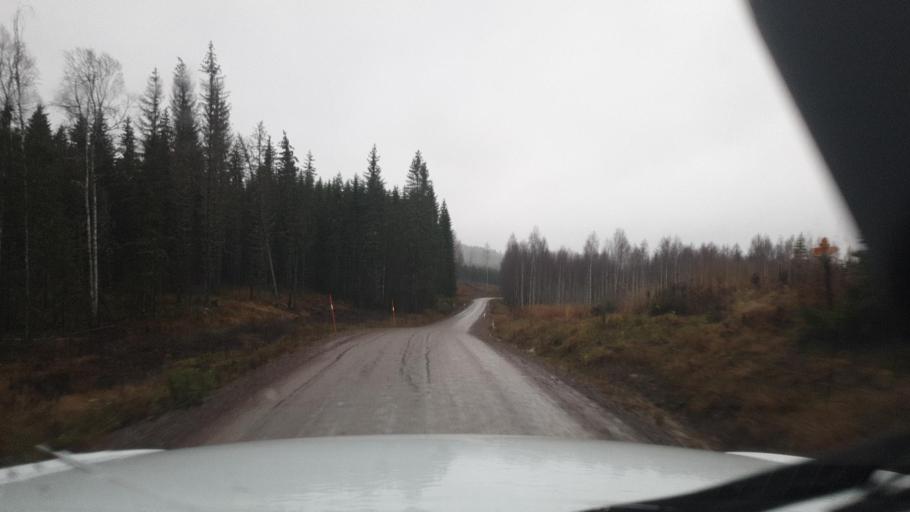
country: SE
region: Vaermland
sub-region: Arvika Kommun
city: Arvika
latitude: 59.9467
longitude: 12.6617
